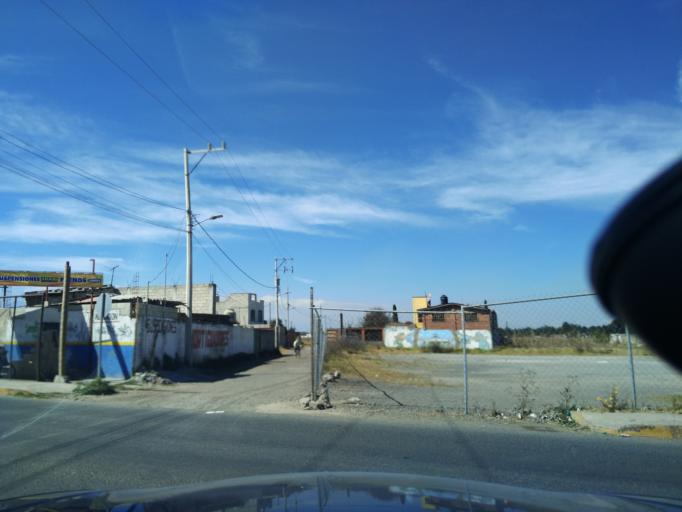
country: MX
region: Morelos
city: Ocoyoacac
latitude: 19.2670
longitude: -99.4660
